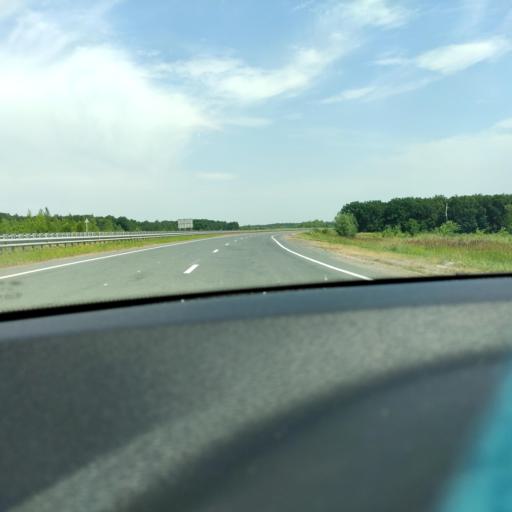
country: RU
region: Samara
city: Petra-Dubrava
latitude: 53.3386
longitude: 50.4358
